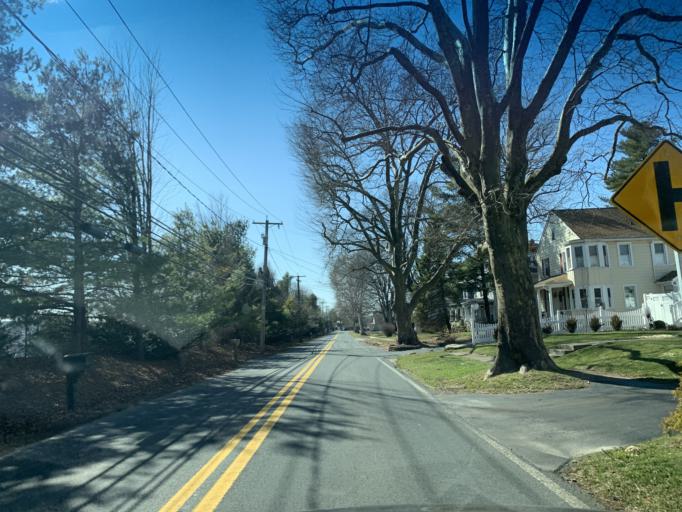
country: US
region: Maryland
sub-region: Carroll County
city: Hampstead
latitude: 39.6008
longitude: -76.8528
